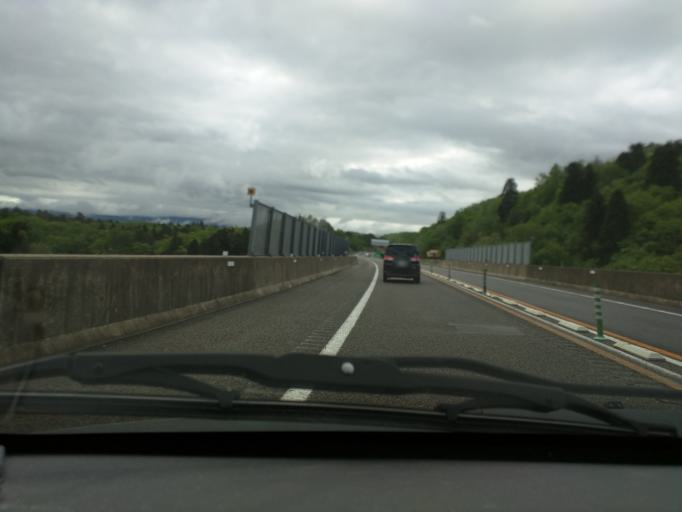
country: JP
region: Niigata
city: Joetsu
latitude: 37.1200
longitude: 138.2145
